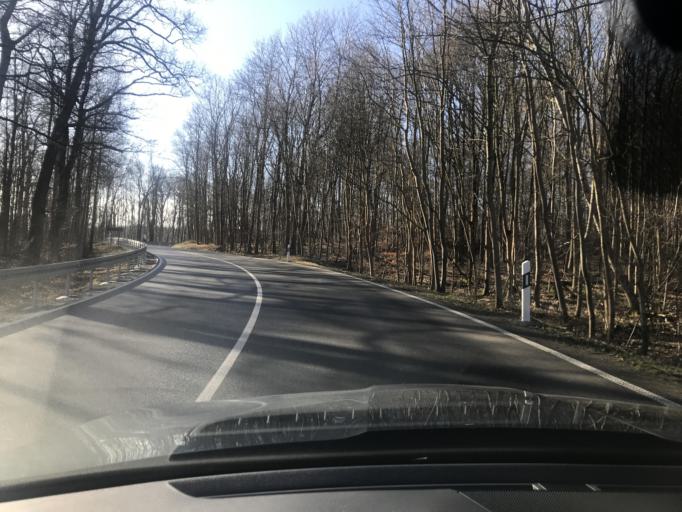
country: DE
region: Saxony-Anhalt
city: Blankenburg
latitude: 51.7858
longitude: 10.9290
